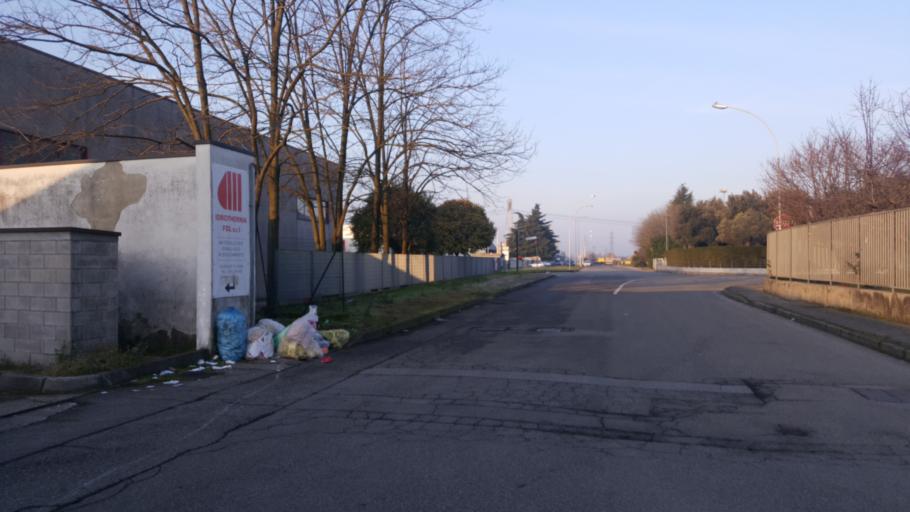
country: IT
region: Lombardy
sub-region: Citta metropolitana di Milano
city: Cassano d'Adda
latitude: 45.5259
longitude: 9.5004
